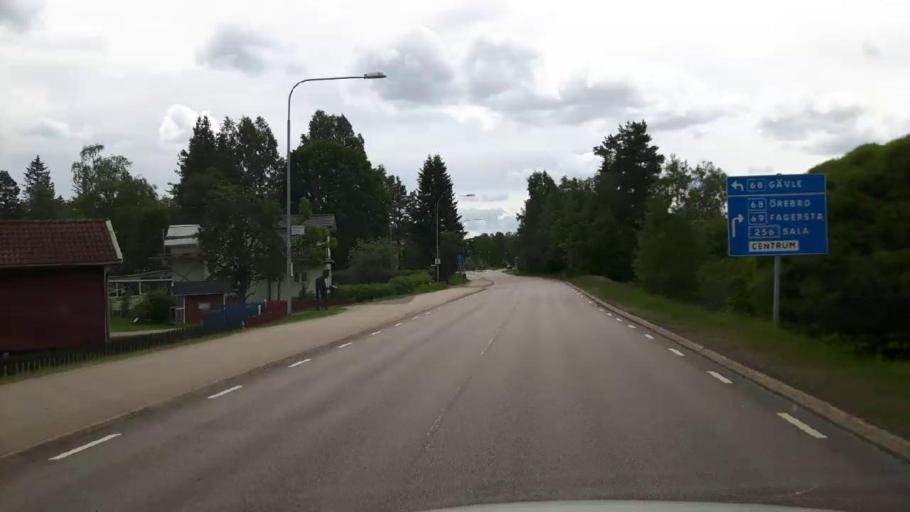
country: SE
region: Vaestmanland
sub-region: Norbergs Kommun
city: Norberg
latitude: 60.0765
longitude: 15.9303
